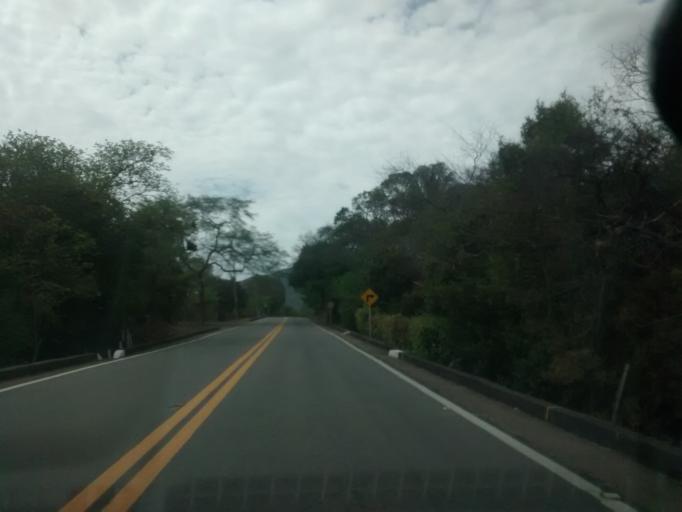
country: CO
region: Cundinamarca
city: Agua de Dios
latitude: 4.4137
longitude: -74.7097
